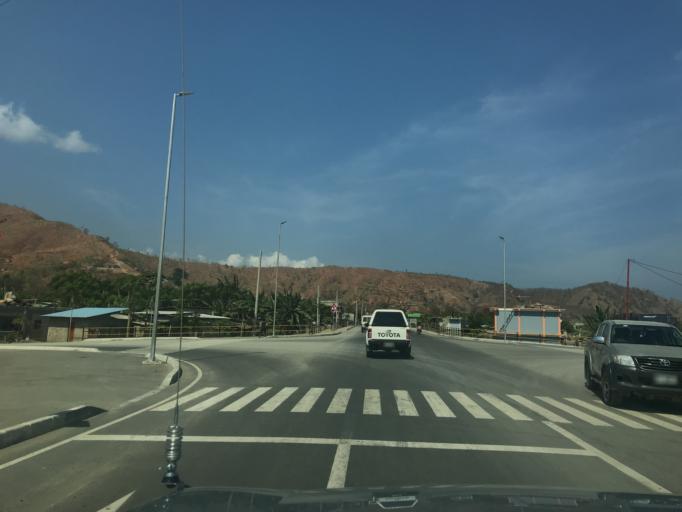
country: TL
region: Dili
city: Dili
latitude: -8.5614
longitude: 125.5328
